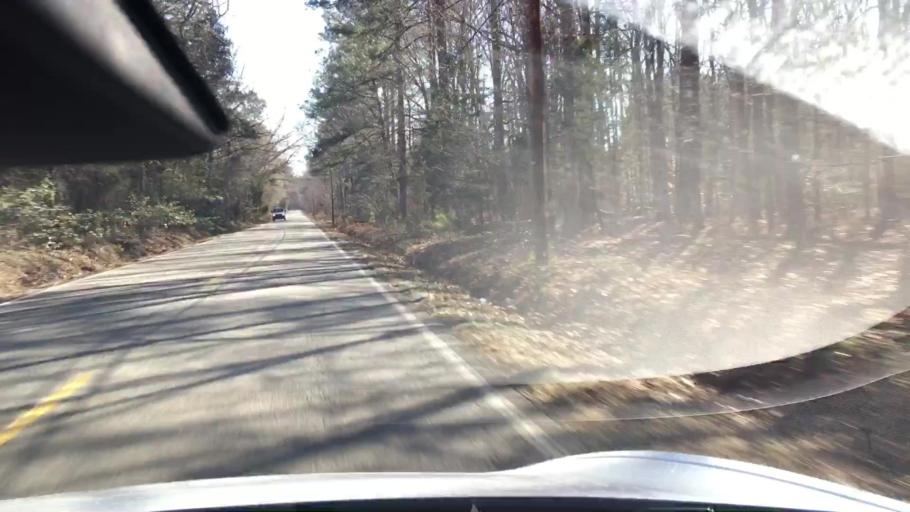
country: US
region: Virginia
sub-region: Henrico County
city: Short Pump
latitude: 37.5821
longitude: -77.7427
